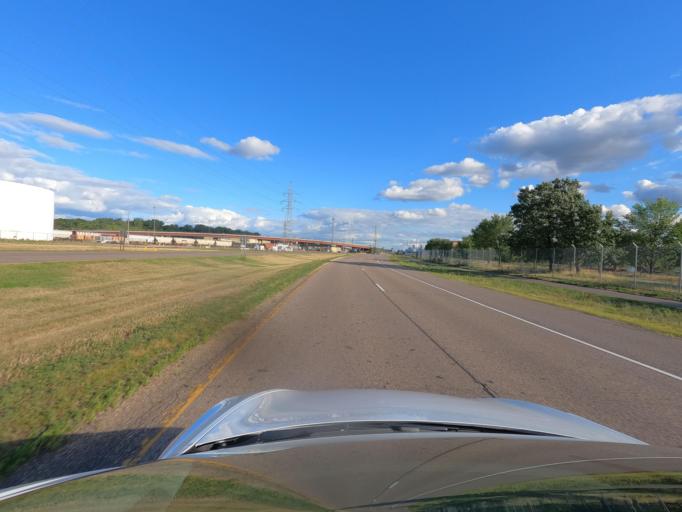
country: US
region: Minnesota
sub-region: Anoka County
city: Columbia Heights
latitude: 45.0484
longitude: -93.2754
